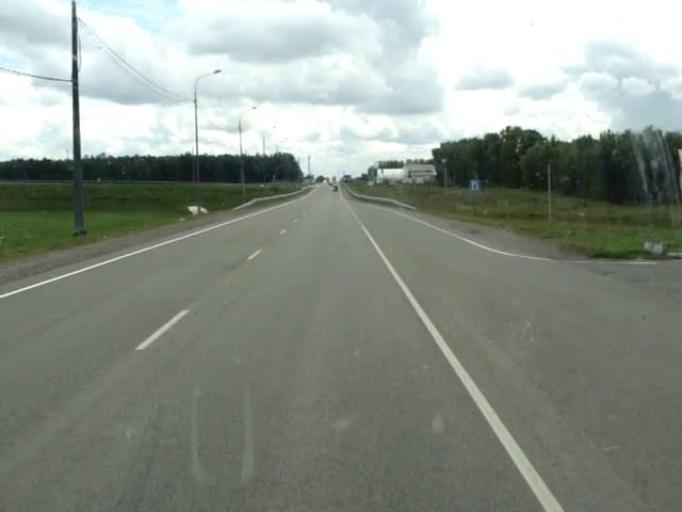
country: RU
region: Altai Krai
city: Zarya
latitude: 52.5788
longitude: 85.1772
